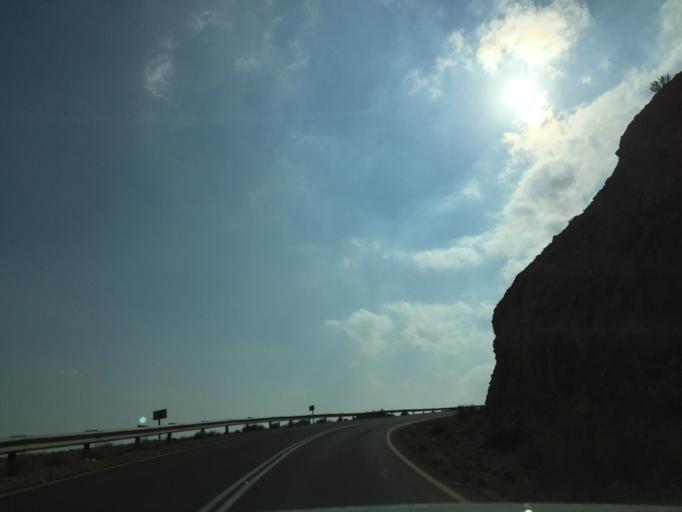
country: IL
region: Southern District
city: `En Boqeq
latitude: 31.3202
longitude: 35.3325
